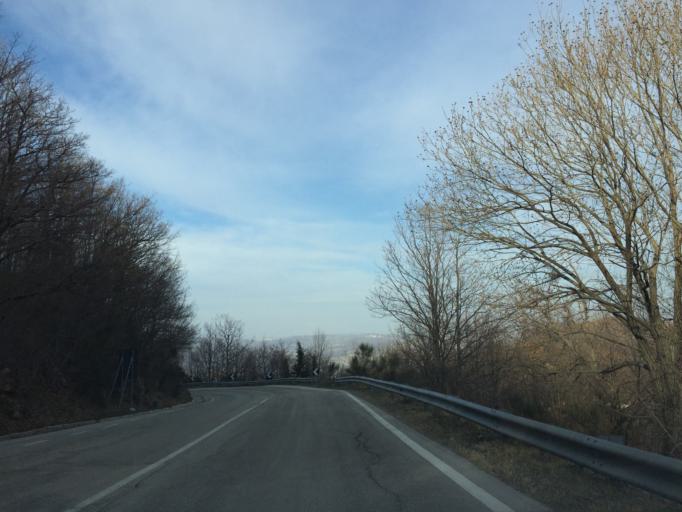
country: IT
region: Molise
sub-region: Provincia di Campobasso
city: San Massimo
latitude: 41.4819
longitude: 14.4091
